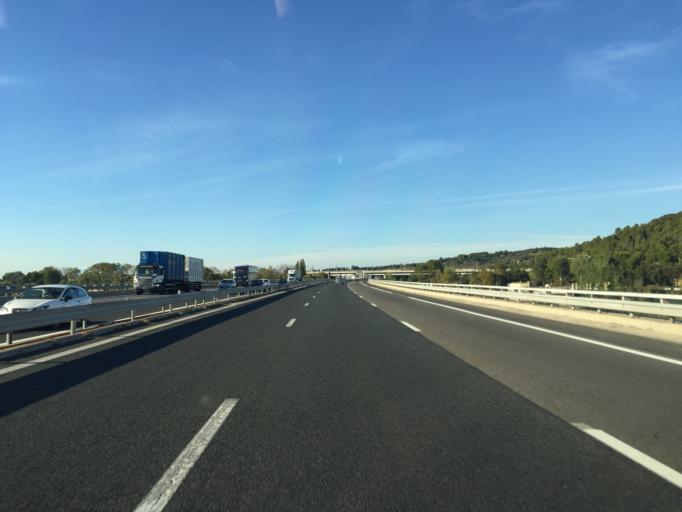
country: FR
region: Provence-Alpes-Cote d'Azur
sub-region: Departement des Bouches-du-Rhone
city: Noves
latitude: 43.8858
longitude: 4.9232
